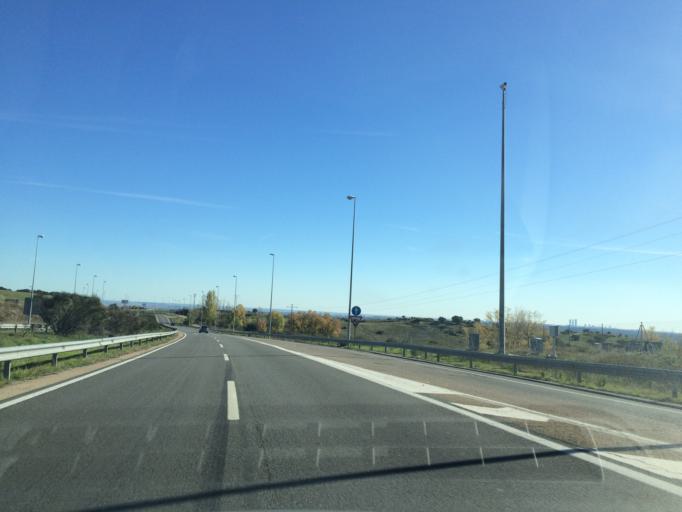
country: ES
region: Madrid
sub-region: Provincia de Madrid
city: Colmenar Viejo
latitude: 40.6569
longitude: -3.7470
